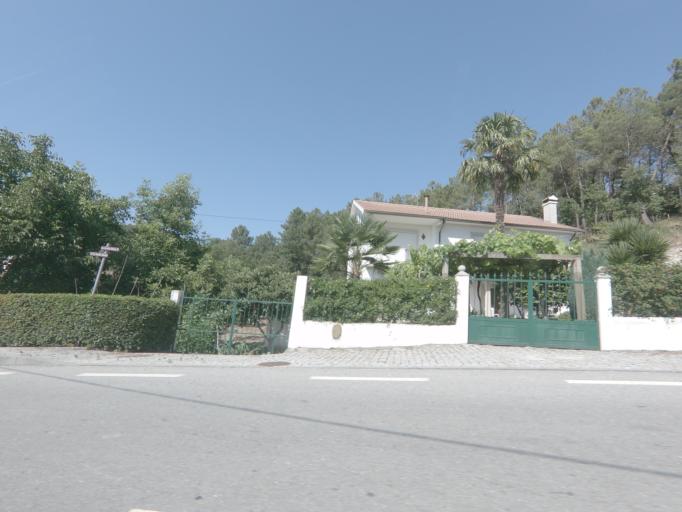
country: PT
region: Viseu
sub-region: Tarouca
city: Tarouca
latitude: 41.0239
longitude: -7.7521
